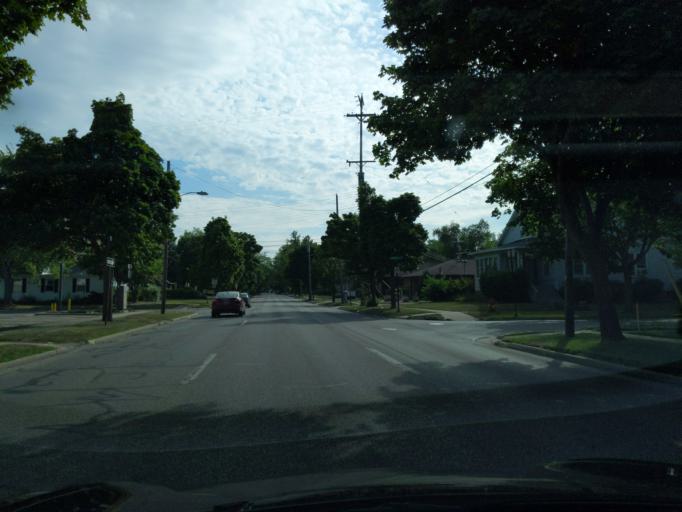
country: US
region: Michigan
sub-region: Midland County
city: Midland
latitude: 43.6249
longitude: -84.2292
